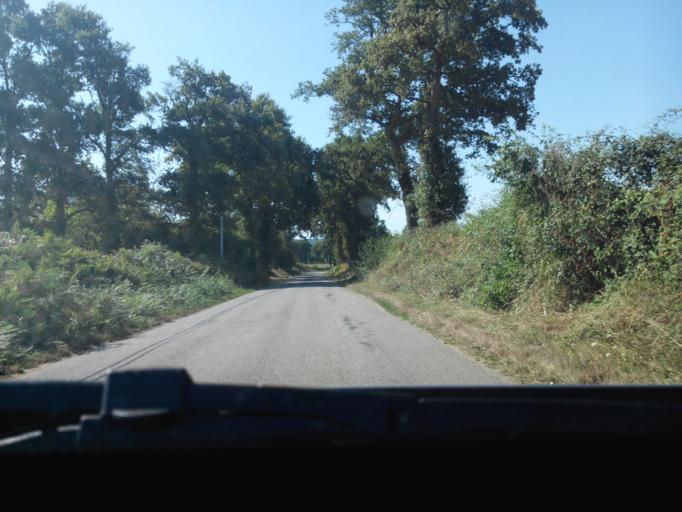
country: FR
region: Poitou-Charentes
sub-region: Departement de la Charente
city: Etagnac
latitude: 45.9569
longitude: 0.7851
